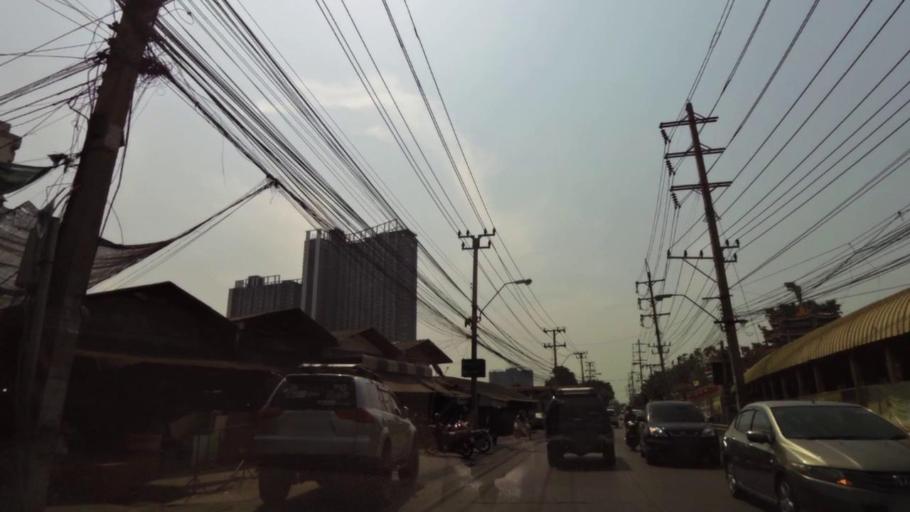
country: TH
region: Samut Prakan
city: Samut Prakan
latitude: 13.6498
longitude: 100.5934
